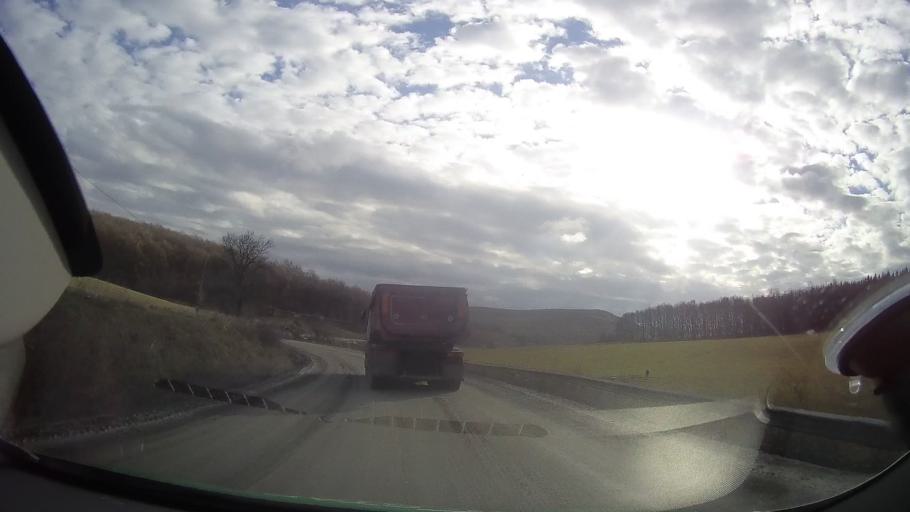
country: RO
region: Cluj
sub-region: Comuna Savadisla
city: Savadisla
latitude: 46.6480
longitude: 23.4622
